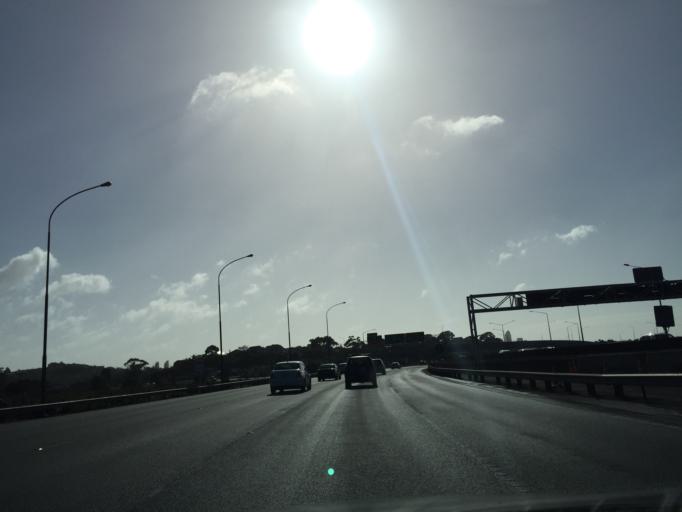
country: NZ
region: Auckland
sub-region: Auckland
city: North Shore
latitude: -36.8161
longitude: 174.7507
